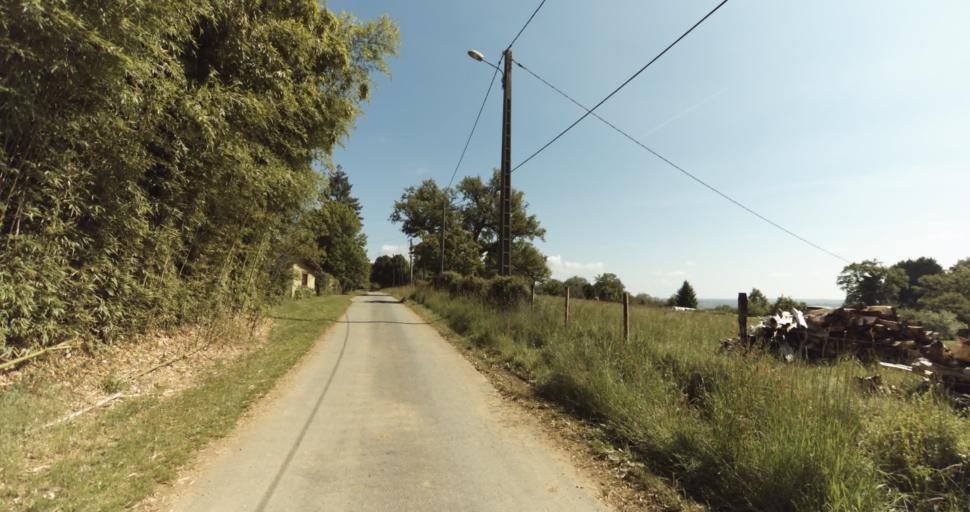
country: FR
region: Limousin
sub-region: Departement de la Haute-Vienne
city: Le Vigen
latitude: 45.7125
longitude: 1.2883
